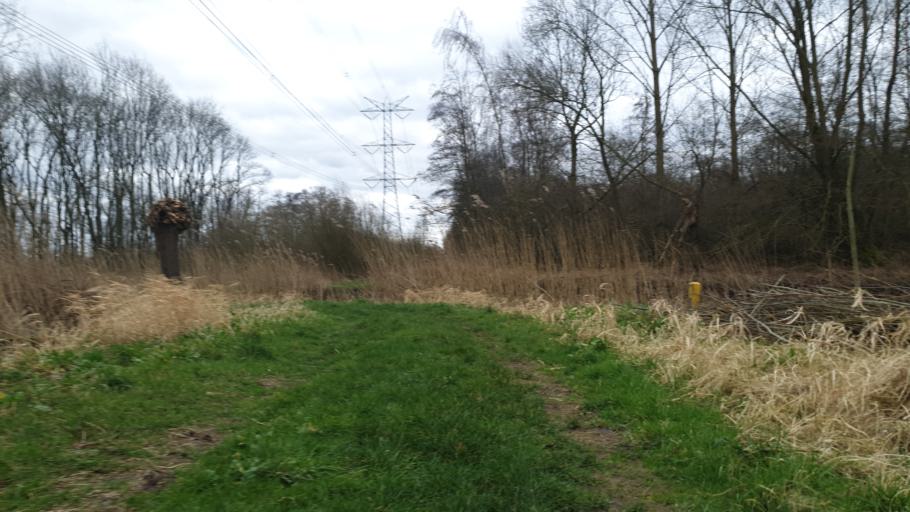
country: NL
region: North Brabant
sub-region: Gemeente Eindhoven
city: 't Hofke
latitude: 51.4654
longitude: 5.5121
